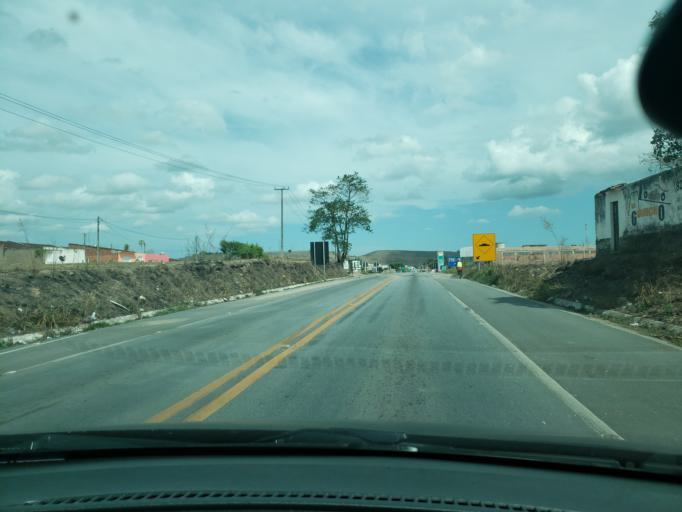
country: BR
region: Alagoas
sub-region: Murici
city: Murici
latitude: -9.3059
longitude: -35.9427
